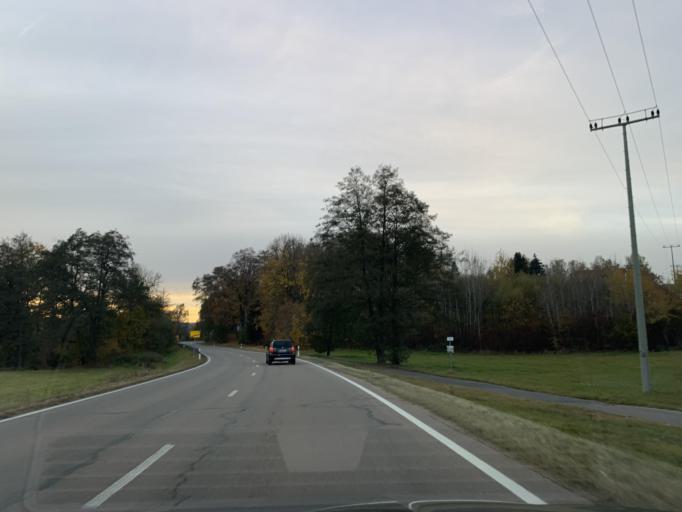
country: DE
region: Bavaria
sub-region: Upper Palatinate
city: Neunburg vorm Wald
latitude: 49.3520
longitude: 12.3820
